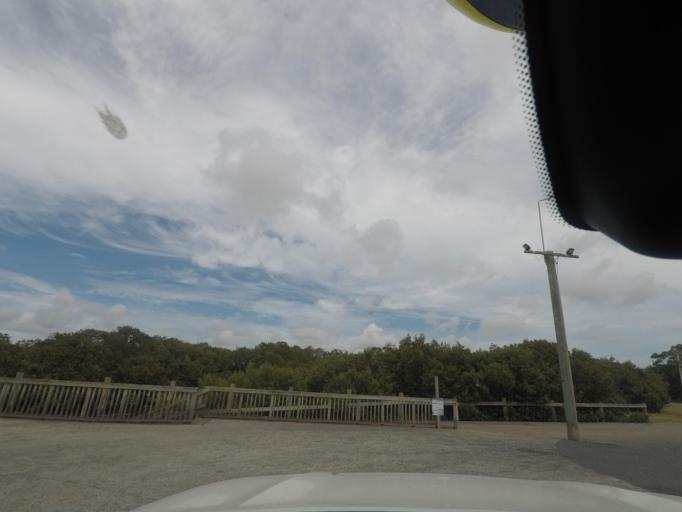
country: NZ
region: Auckland
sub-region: Auckland
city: Parakai
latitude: -36.6583
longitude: 174.4404
